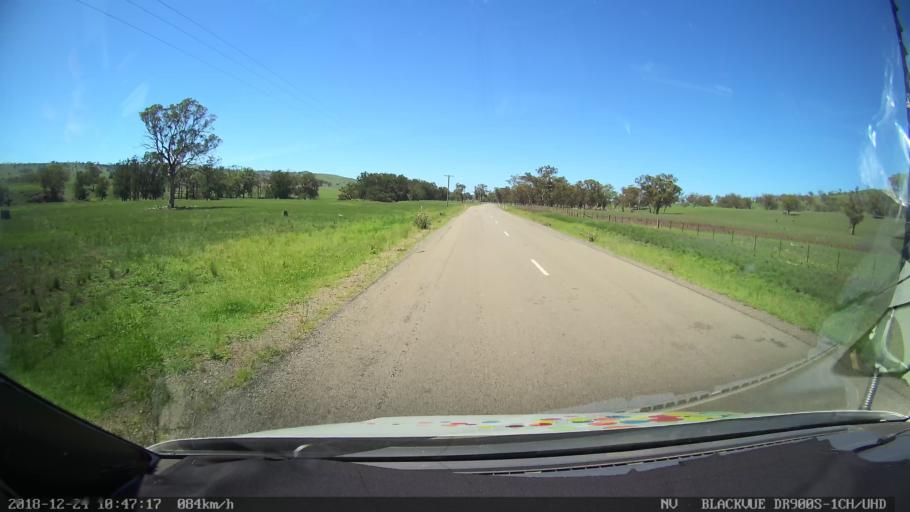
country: AU
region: New South Wales
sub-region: Upper Hunter Shire
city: Merriwa
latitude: -31.9227
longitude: 150.4295
